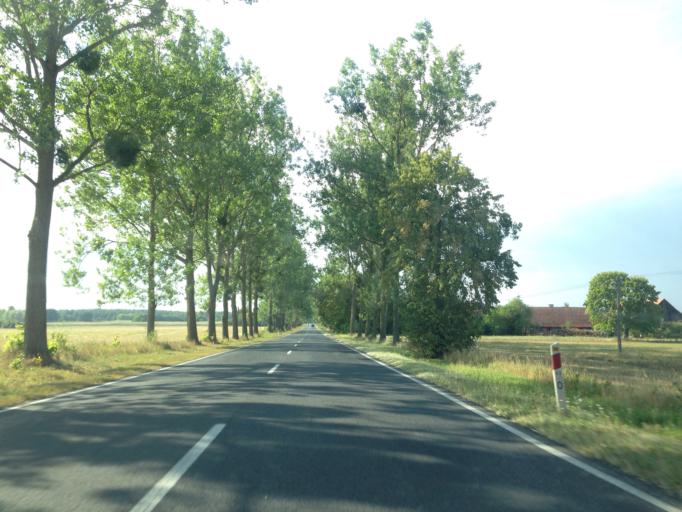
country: PL
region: Kujawsko-Pomorskie
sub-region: Powiat swiecki
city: Bukowiec
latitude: 53.4589
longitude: 18.1920
